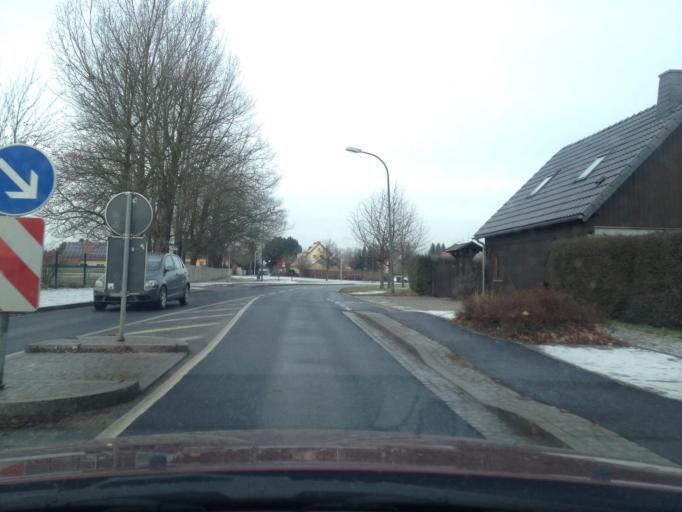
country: DE
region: Saxony
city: Goerlitz
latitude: 51.1396
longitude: 14.9493
